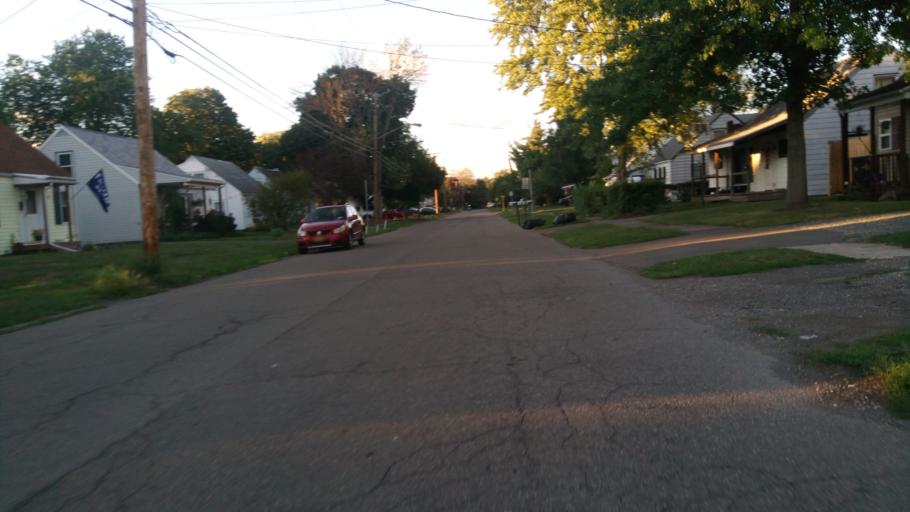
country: US
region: New York
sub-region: Chemung County
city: Southport
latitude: 42.0616
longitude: -76.8019
